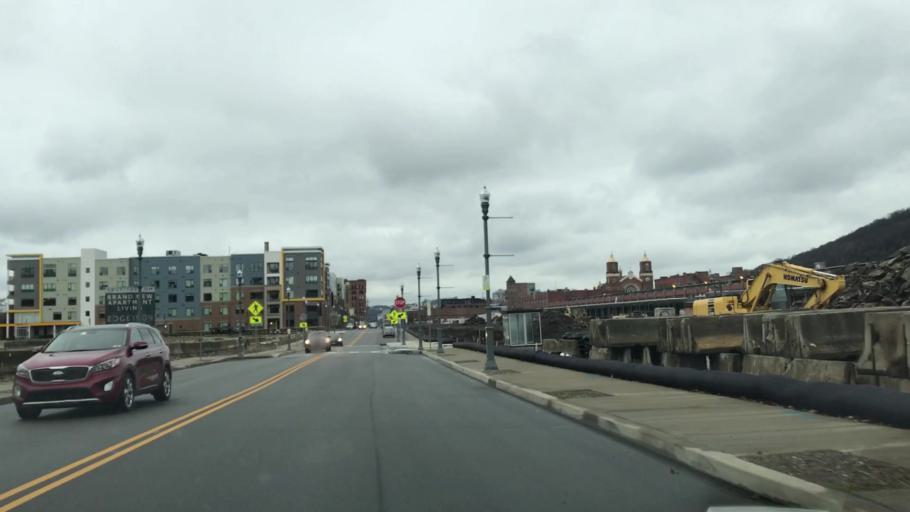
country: US
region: Pennsylvania
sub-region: Allegheny County
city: Pittsburgh
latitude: 40.4507
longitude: -79.9881
